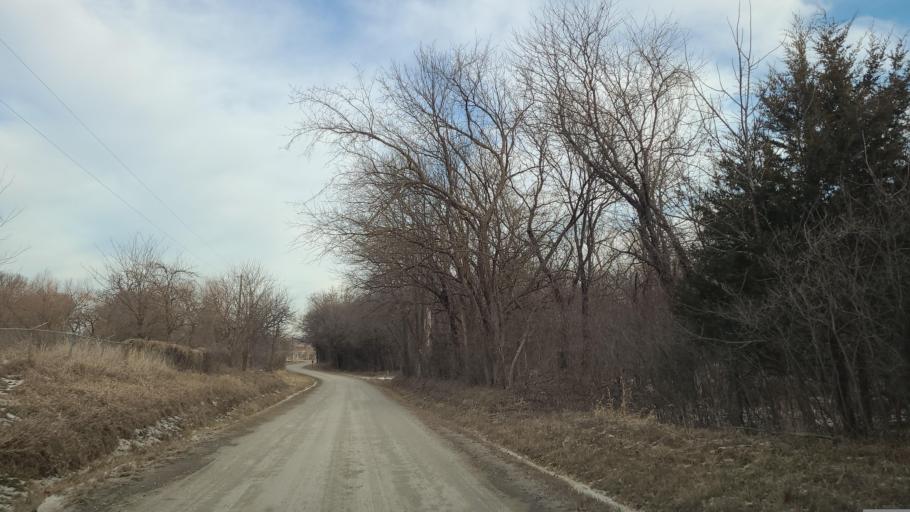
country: US
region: Kansas
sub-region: Jefferson County
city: Oskaloosa
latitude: 39.0548
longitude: -95.4098
